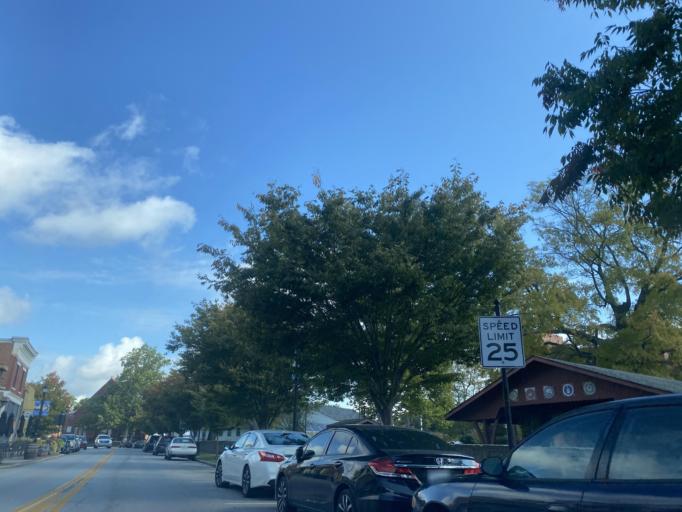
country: US
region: Kentucky
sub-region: Campbell County
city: Fort Thomas
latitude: 39.0647
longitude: -84.4465
